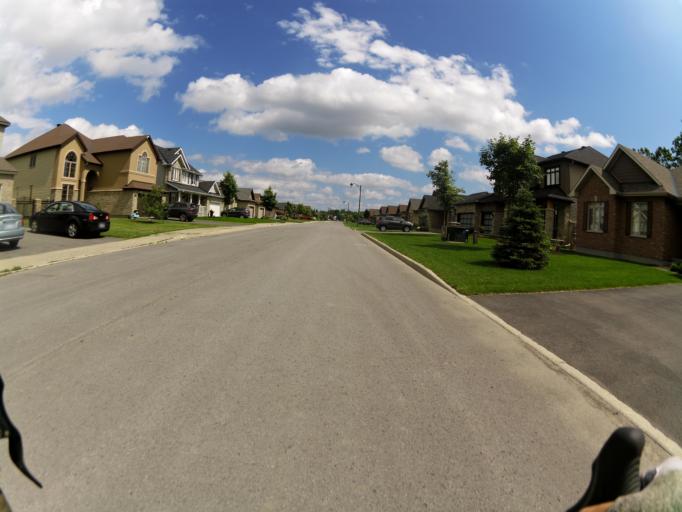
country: CA
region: Ontario
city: Bells Corners
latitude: 45.1950
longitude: -75.8492
